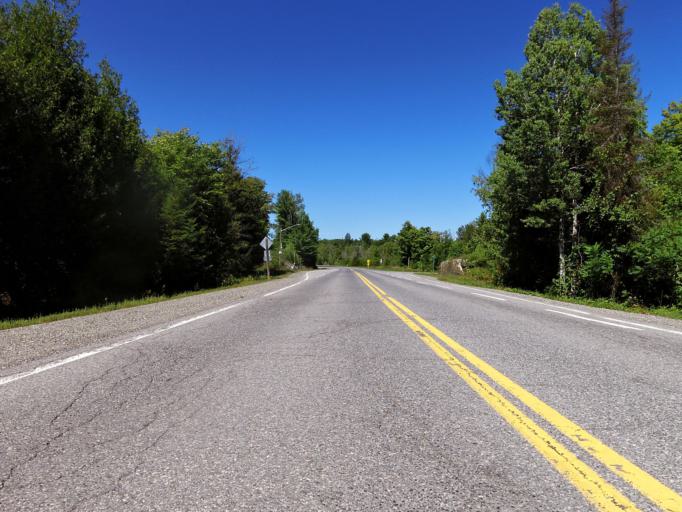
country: CA
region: Ontario
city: Arnprior
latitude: 45.1592
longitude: -76.5192
